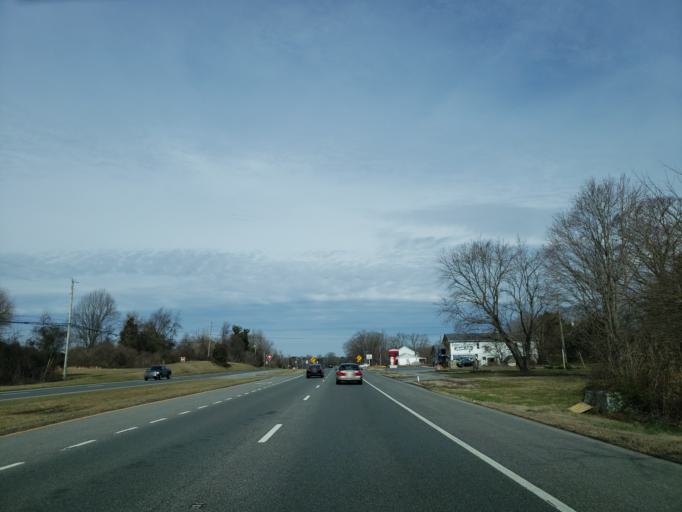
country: US
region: Delaware
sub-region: Kent County
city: Cheswold
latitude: 39.2392
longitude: -75.5849
